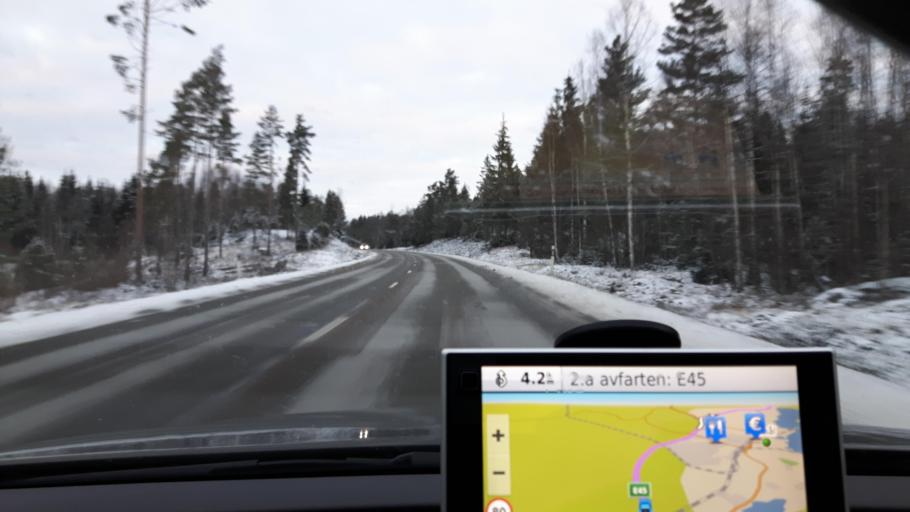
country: SE
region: Vaestra Goetaland
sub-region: Amals Kommun
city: Amal
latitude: 59.0206
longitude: 12.6857
